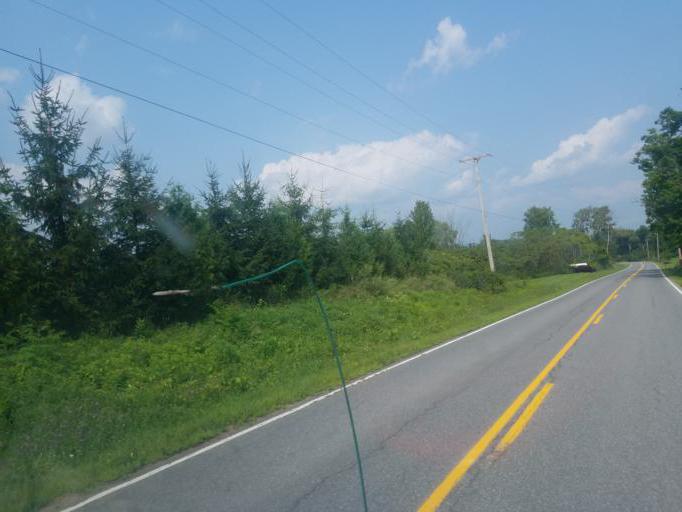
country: US
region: New York
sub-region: Montgomery County
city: Fonda
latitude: 42.9109
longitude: -74.3316
